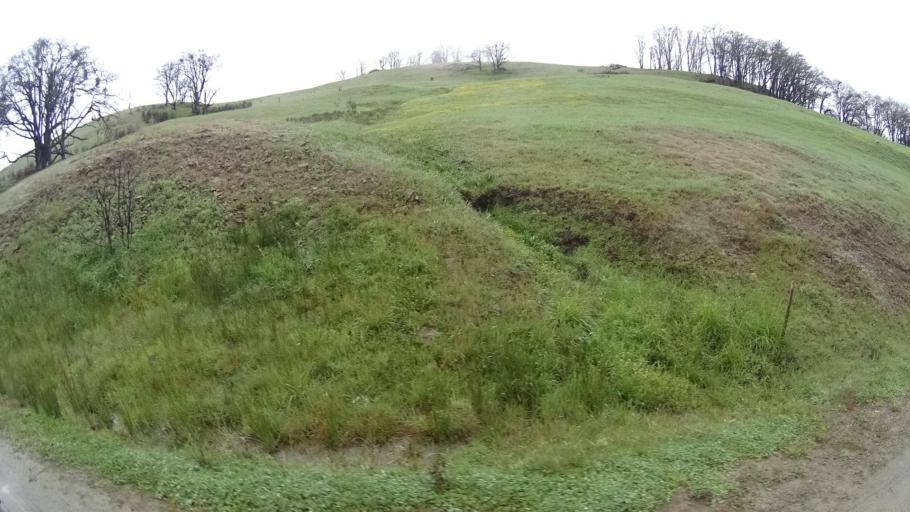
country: US
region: California
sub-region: Humboldt County
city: Westhaven-Moonstone
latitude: 41.1465
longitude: -123.8886
